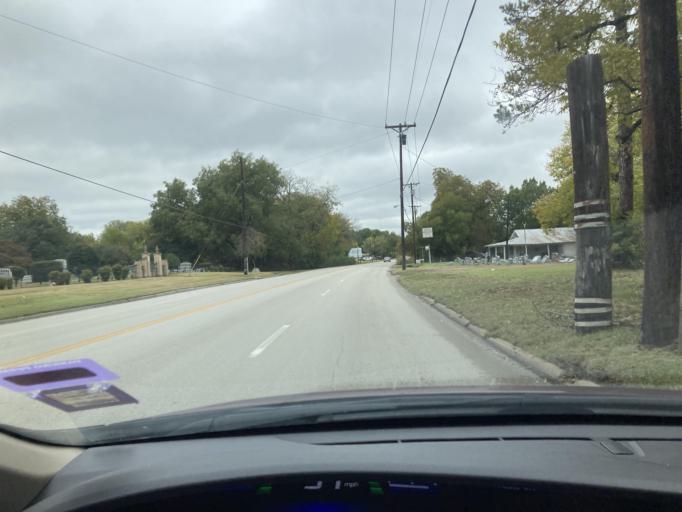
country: US
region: Texas
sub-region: Navarro County
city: Corsicana
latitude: 32.0855
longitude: -96.4900
